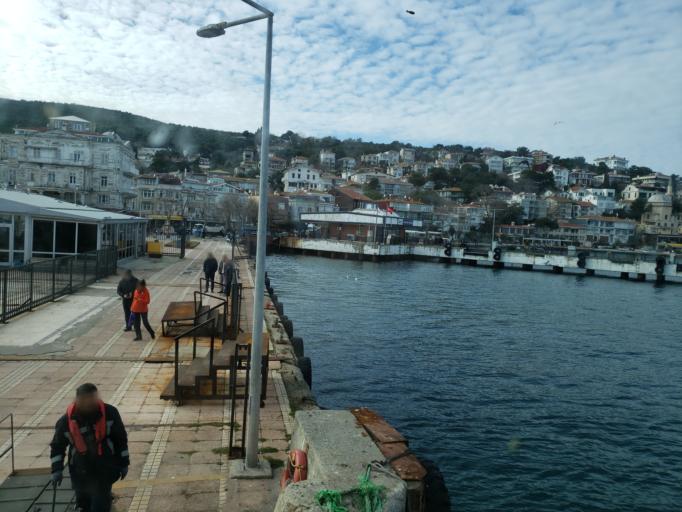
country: TR
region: Istanbul
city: Adalan
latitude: 40.8812
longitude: 29.0707
